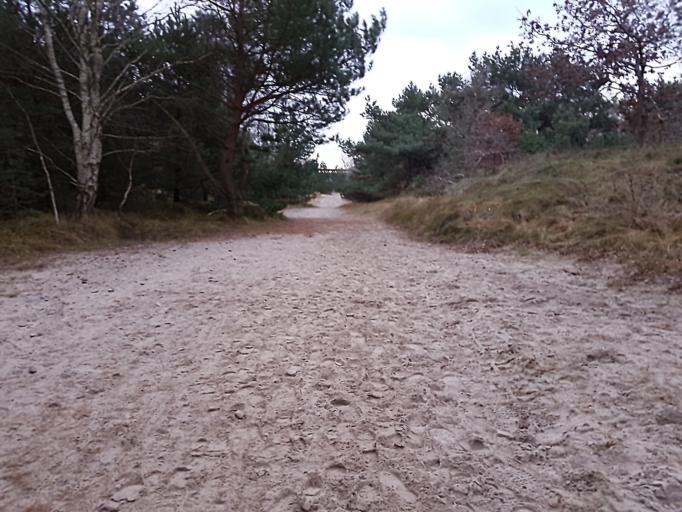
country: DE
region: Mecklenburg-Vorpommern
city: Ostseebad Binz
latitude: 54.4417
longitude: 13.5744
